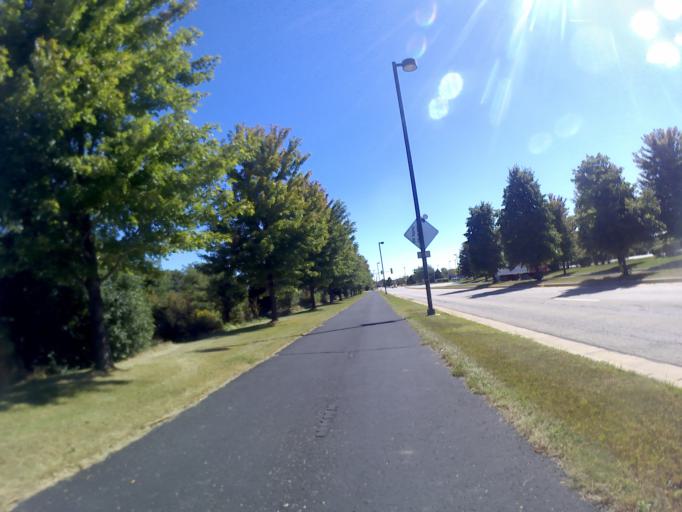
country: US
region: Illinois
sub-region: Cook County
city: Lemont
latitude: 41.7048
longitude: -88.0224
